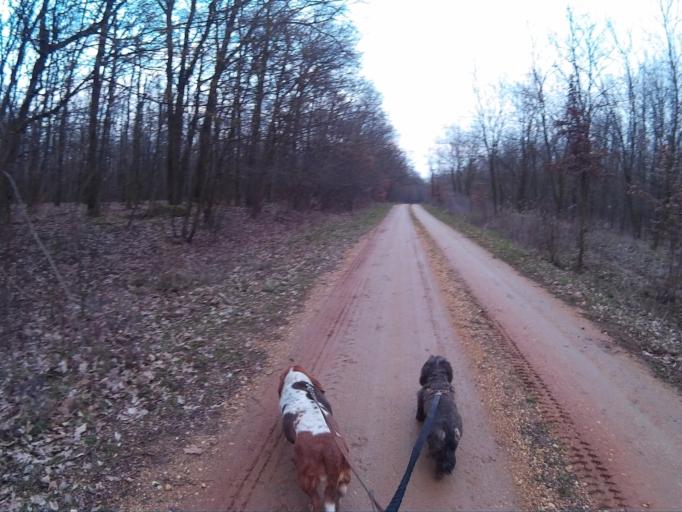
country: HU
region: Vas
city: Janoshaza
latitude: 47.1257
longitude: 17.0475
